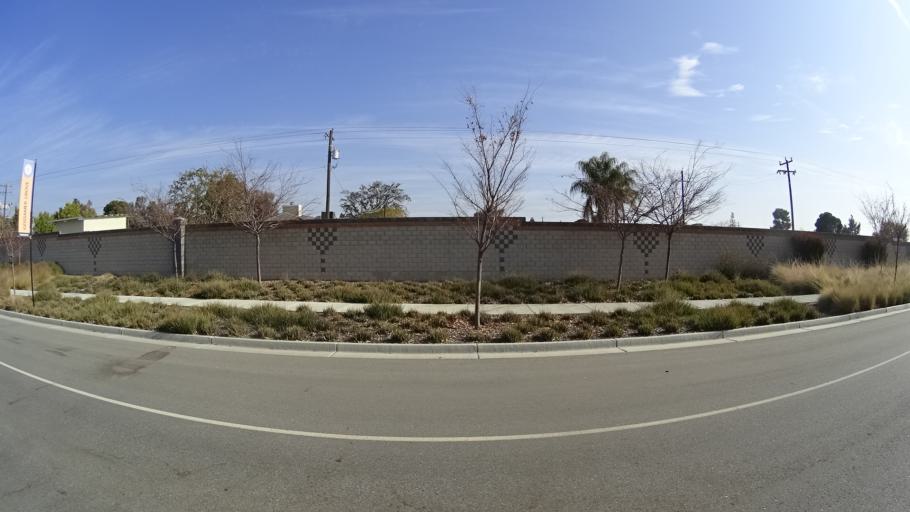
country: US
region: California
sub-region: Kern County
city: Greenacres
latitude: 35.4435
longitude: -119.1099
